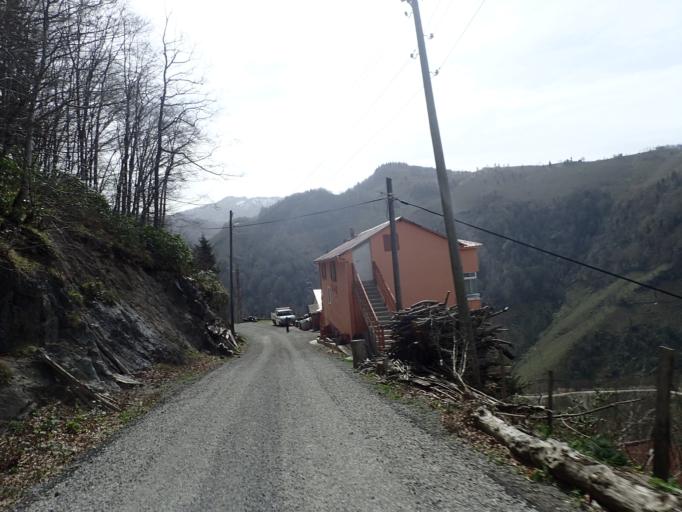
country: TR
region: Ordu
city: Kabaduz
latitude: 40.7804
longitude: 37.8991
